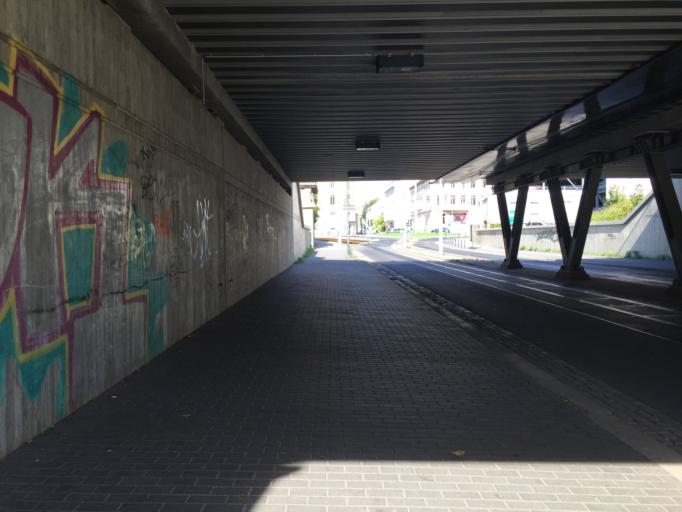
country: DE
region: Saxony
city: Goerlitz
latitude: 51.1458
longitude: 14.9813
